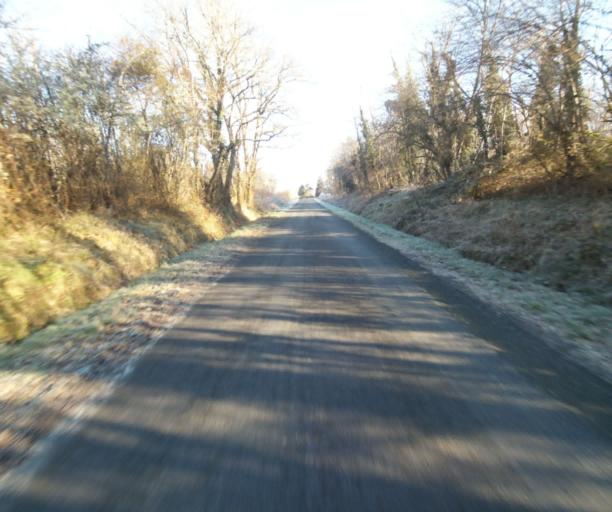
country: FR
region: Aquitaine
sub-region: Departement des Landes
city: Gabarret
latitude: 44.1108
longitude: 0.0793
